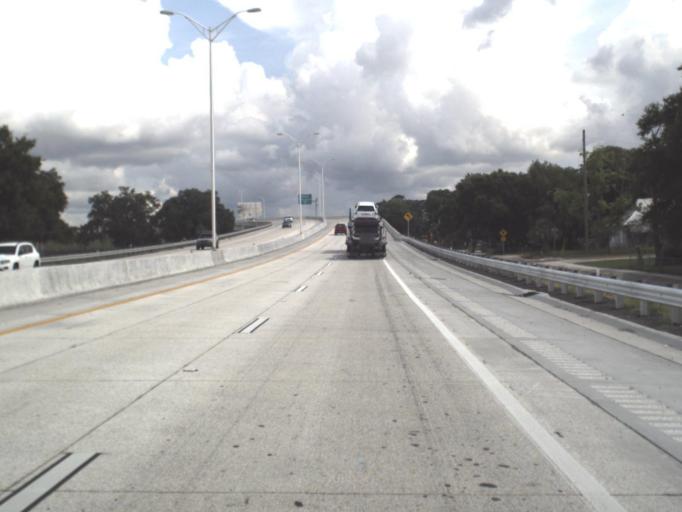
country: US
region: Florida
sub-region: Duval County
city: Jacksonville
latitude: 30.3512
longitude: -81.6368
